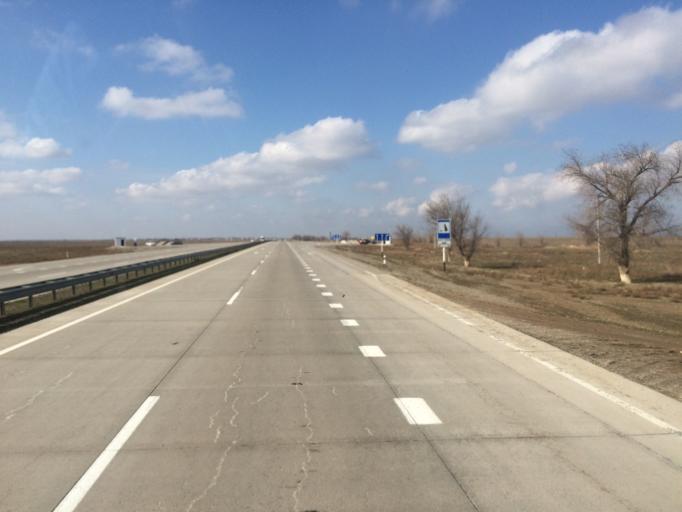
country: KZ
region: Ongtustik Qazaqstan
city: Temirlanovka
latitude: 42.8442
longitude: 69.0979
